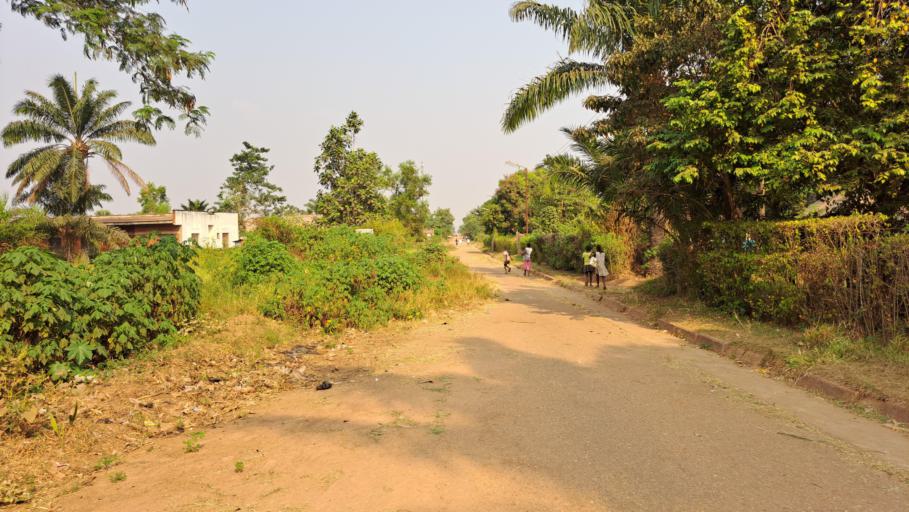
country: CD
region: Kasai-Oriental
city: Mbuji-Mayi
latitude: -6.1368
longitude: 23.5895
